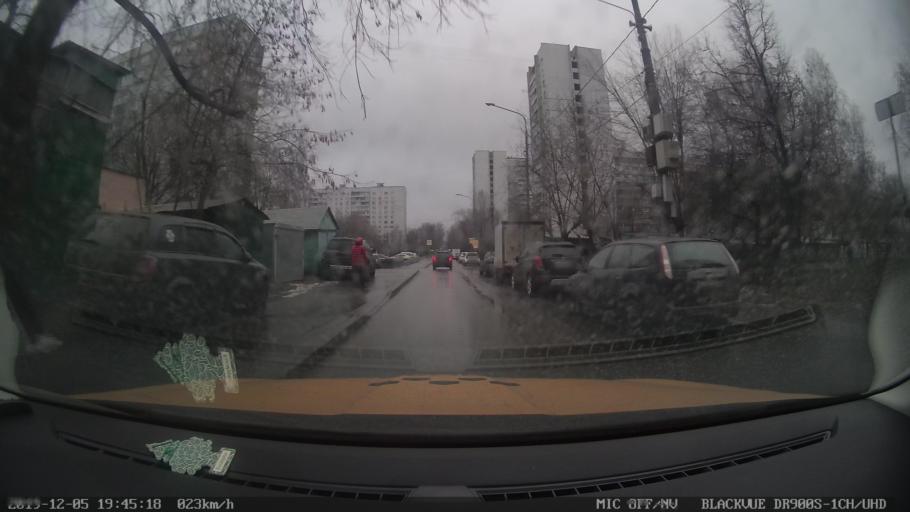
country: RU
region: Moscow
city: Lianozovo
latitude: 55.9028
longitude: 37.5769
